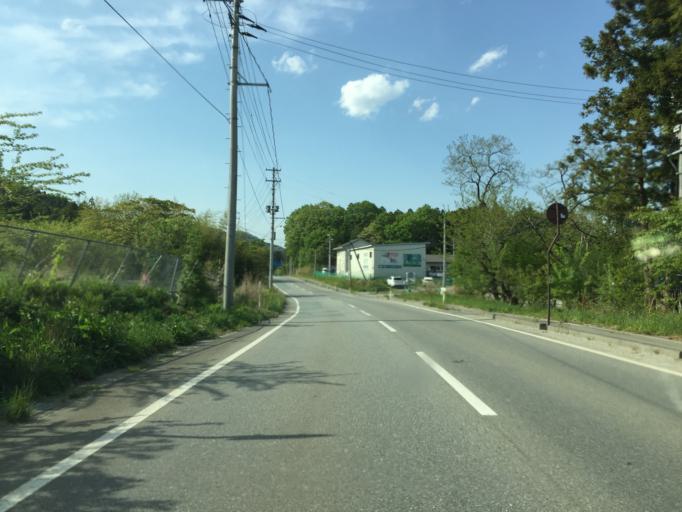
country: JP
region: Fukushima
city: Namie
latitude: 37.3770
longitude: 140.9583
